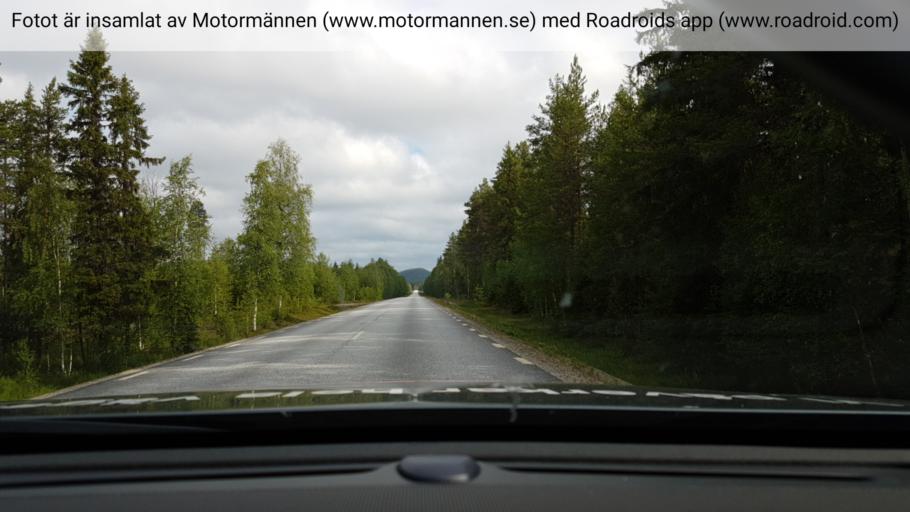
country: SE
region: Vaesterbotten
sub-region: Vindelns Kommun
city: Vindeln
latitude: 64.4004
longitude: 19.3731
